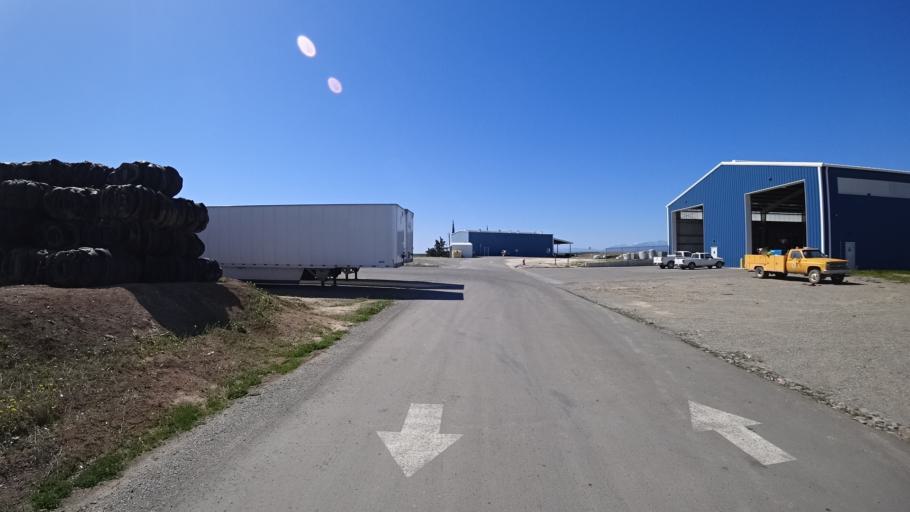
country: US
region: California
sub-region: Glenn County
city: Willows
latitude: 39.6326
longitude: -122.2757
